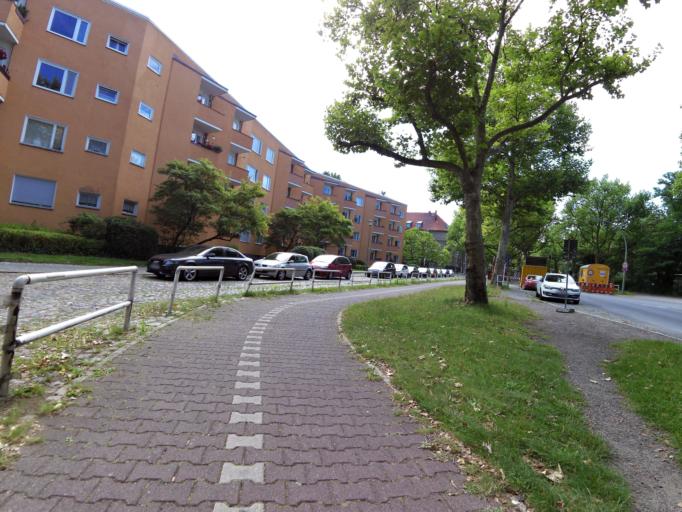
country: DE
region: Berlin
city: Lankwitz
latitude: 52.4293
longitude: 13.3469
